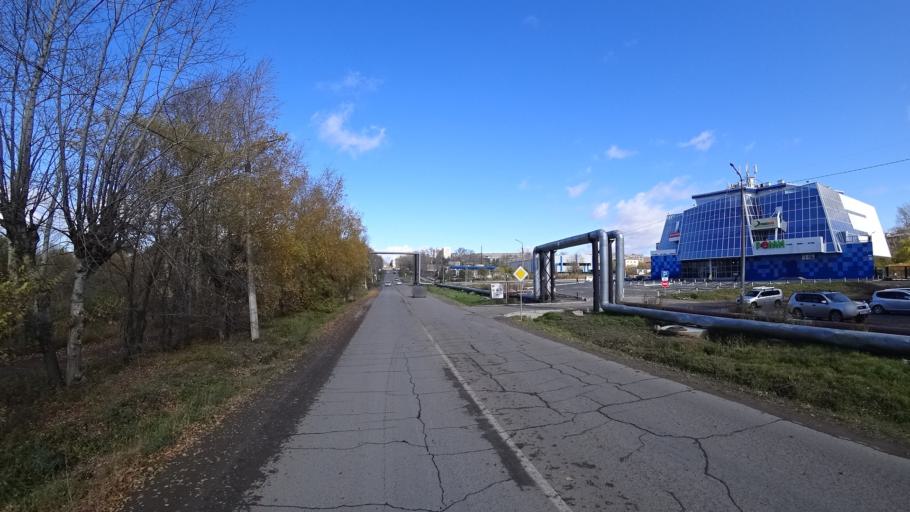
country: RU
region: Khabarovsk Krai
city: Amursk
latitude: 50.2259
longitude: 136.9015
